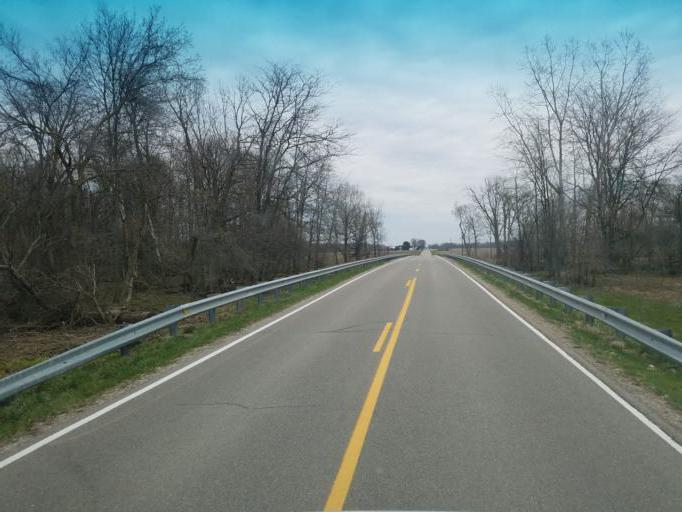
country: US
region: Ohio
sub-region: Crawford County
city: Bucyrus
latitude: 40.8920
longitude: -83.0232
